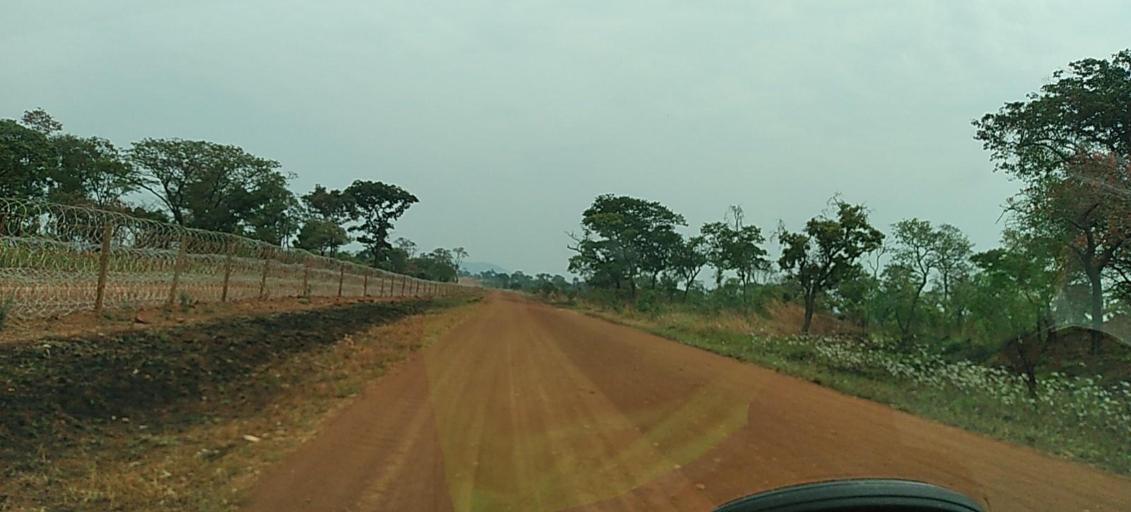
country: ZM
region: North-Western
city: Kansanshi
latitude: -12.0889
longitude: 26.4853
